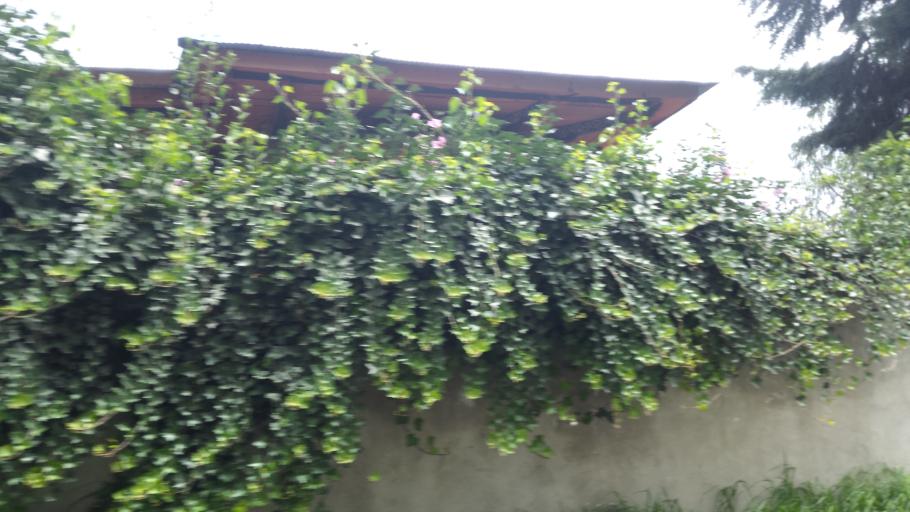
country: BT
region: Thimphu
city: Thimphu
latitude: 27.4740
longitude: 89.6301
